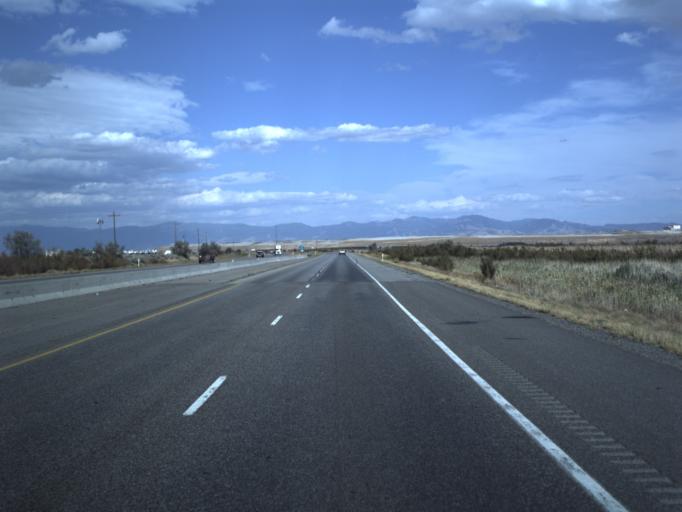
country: US
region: Utah
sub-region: Salt Lake County
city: Magna
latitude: 40.7286
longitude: -112.2119
